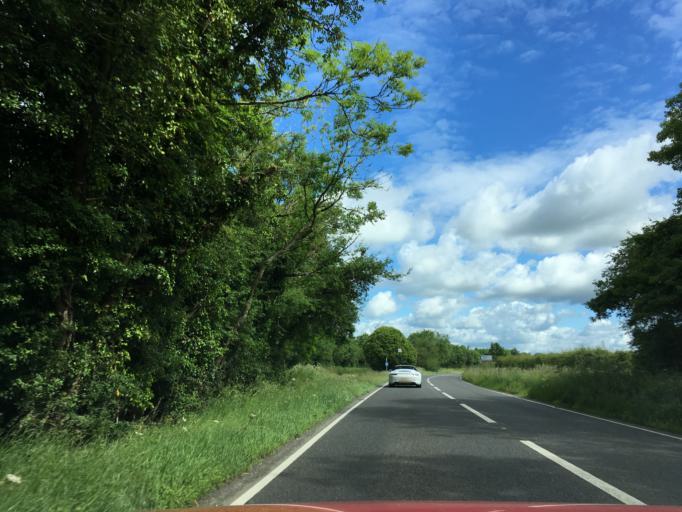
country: GB
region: England
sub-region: Gloucestershire
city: Lechlade
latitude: 51.7165
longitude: -1.6786
